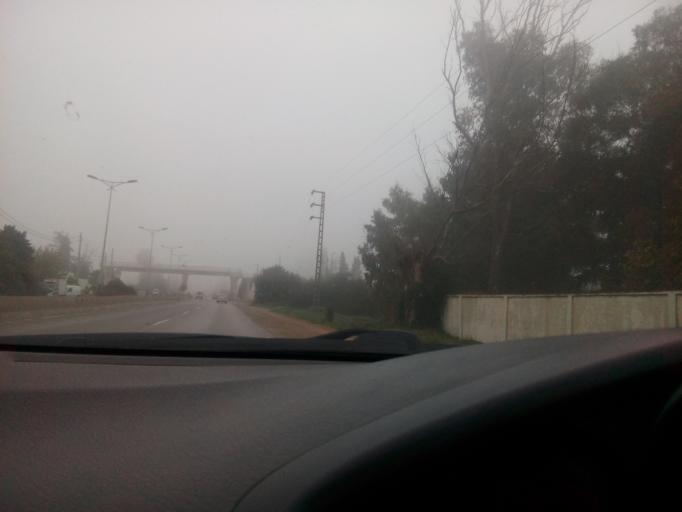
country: DZ
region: Oran
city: Bou Tlelis
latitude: 35.5768
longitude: -0.8459
